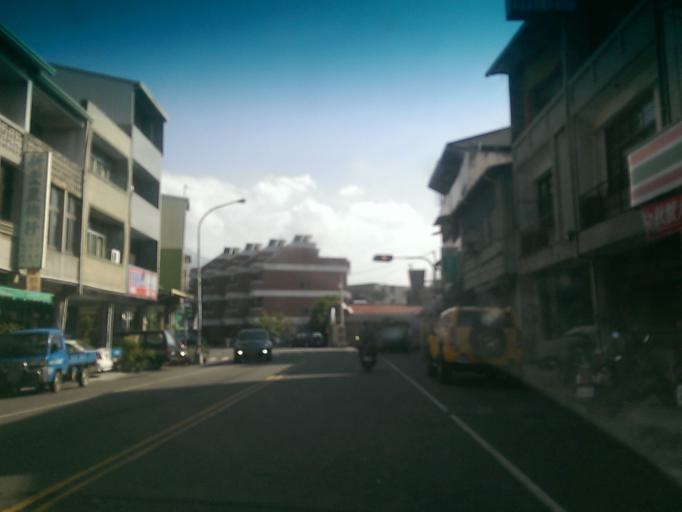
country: TW
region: Taiwan
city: Lugu
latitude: 23.8109
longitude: 120.8557
